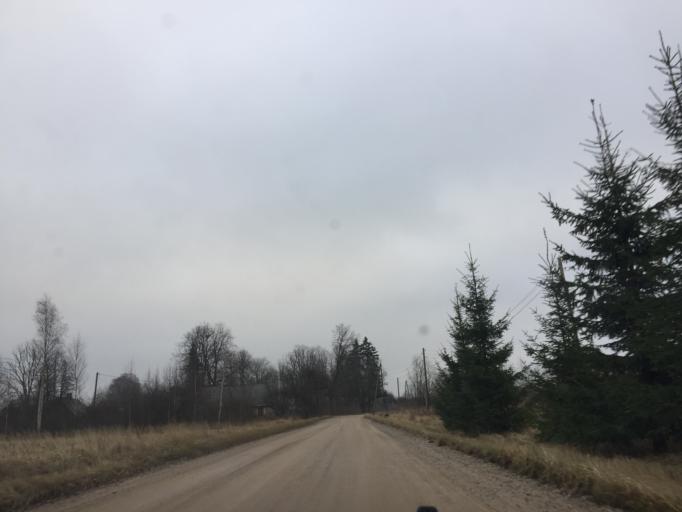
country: LV
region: Limbazu Rajons
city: Limbazi
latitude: 57.5963
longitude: 24.5159
